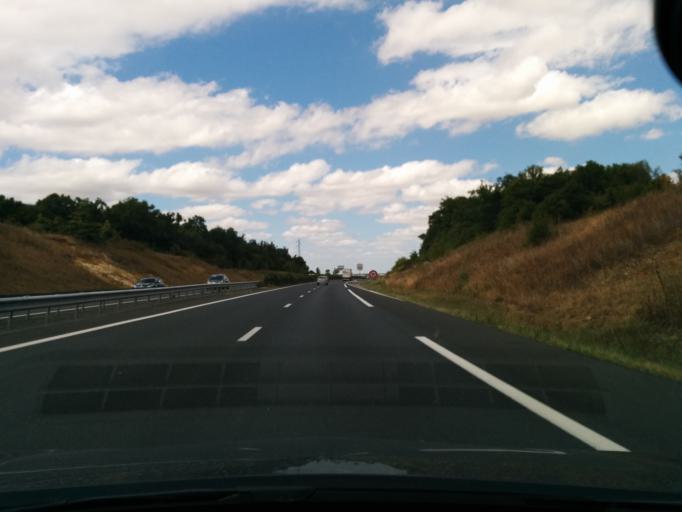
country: FR
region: Centre
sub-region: Departement de l'Indre
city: Saint-Maur
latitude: 46.7953
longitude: 1.6184
